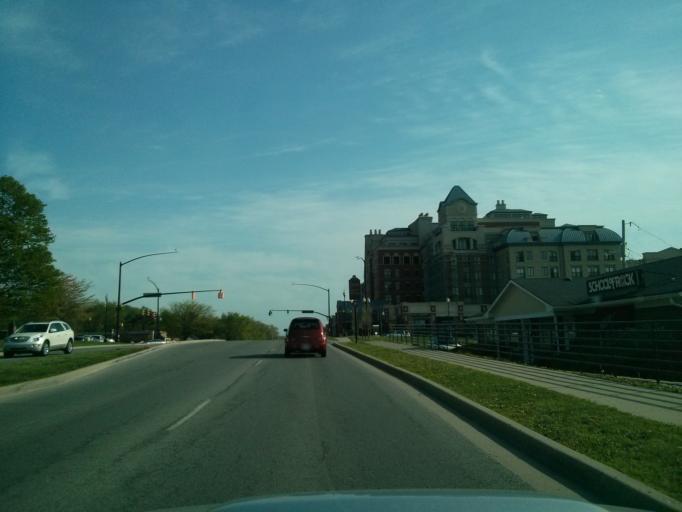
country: US
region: Indiana
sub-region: Hamilton County
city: Carmel
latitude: 39.9716
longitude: -86.1271
